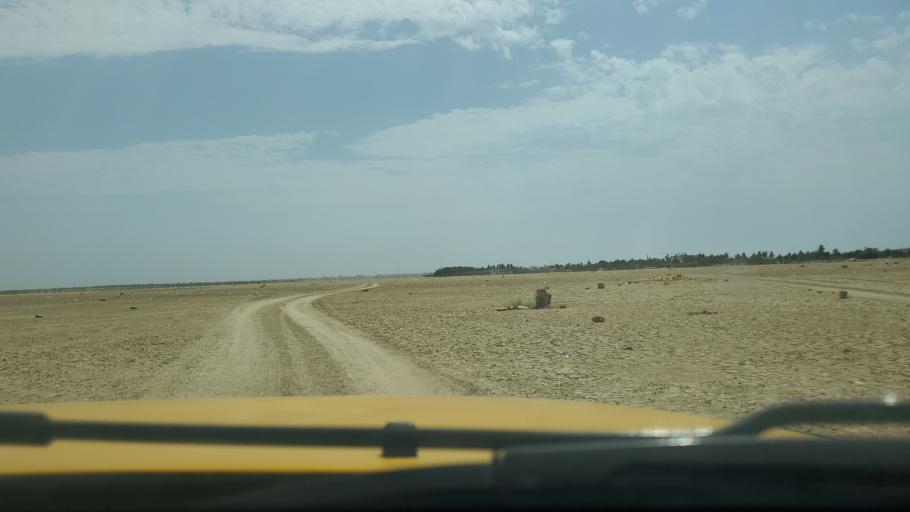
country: SN
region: Saint-Louis
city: Saint-Louis
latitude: 16.0309
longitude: -16.4616
